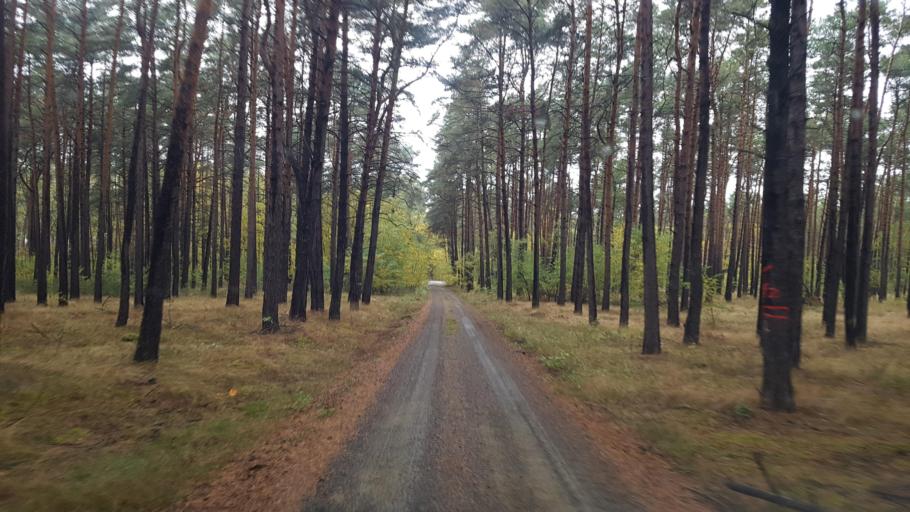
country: DE
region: Brandenburg
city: Schlieben
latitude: 51.7422
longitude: 13.3388
